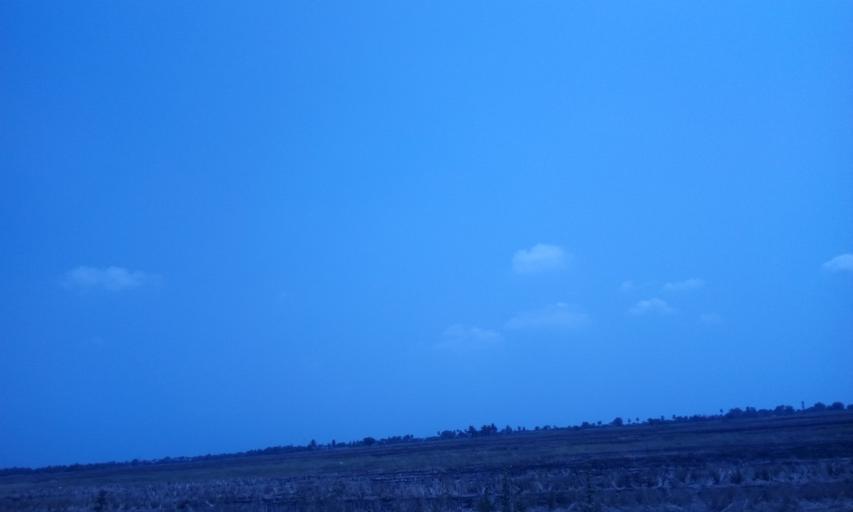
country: TH
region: Chachoengsao
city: Bang Nam Priao
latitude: 13.9556
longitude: 100.9712
